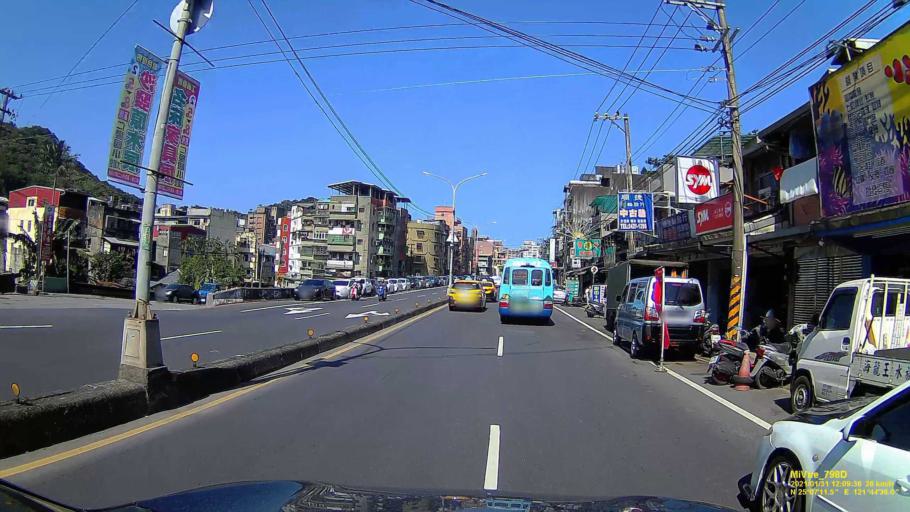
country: TW
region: Taiwan
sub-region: Keelung
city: Keelung
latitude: 25.1201
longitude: 121.7433
